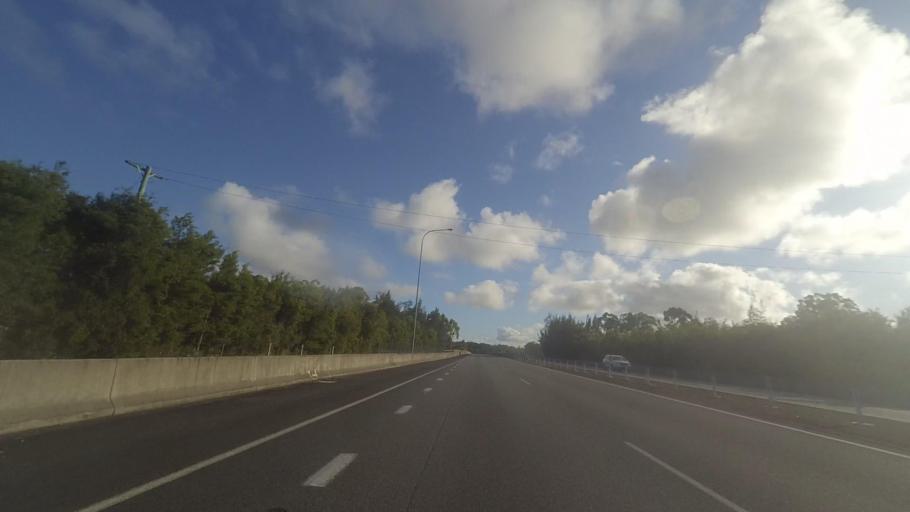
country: AU
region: New South Wales
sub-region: Great Lakes
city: Nabiac
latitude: -32.1034
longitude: 152.3747
